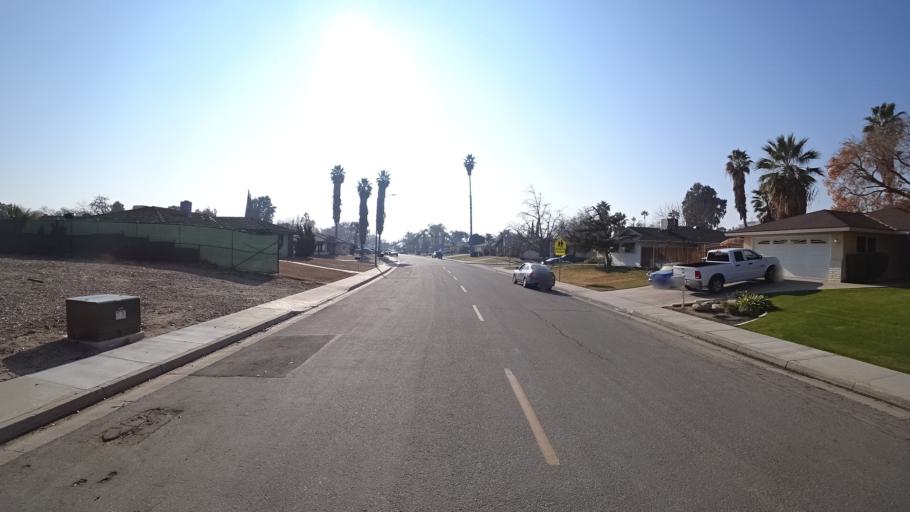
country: US
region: California
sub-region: Kern County
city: Bakersfield
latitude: 35.3629
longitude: -119.0534
